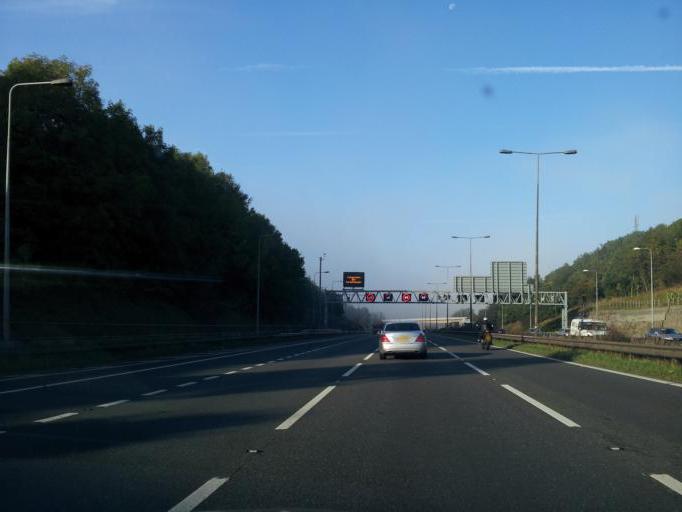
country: GB
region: England
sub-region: City and Borough of Leeds
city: Drighlington
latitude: 53.7451
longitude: -1.6568
